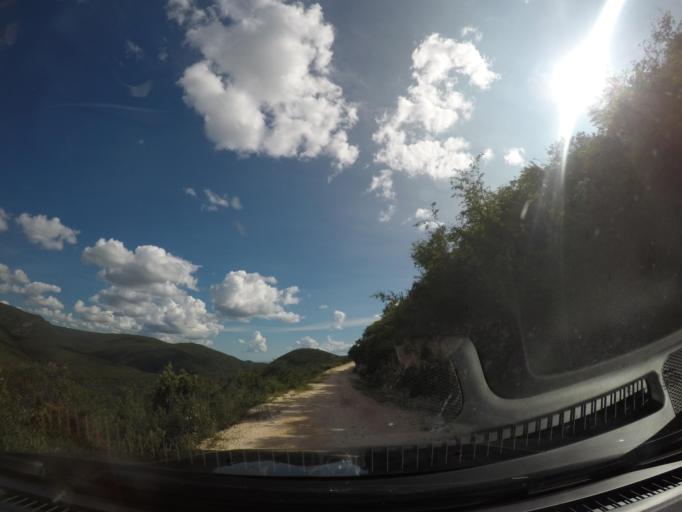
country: BR
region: Bahia
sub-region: Barra Da Estiva
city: Barra da Estiva
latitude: -13.2124
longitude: -41.5918
